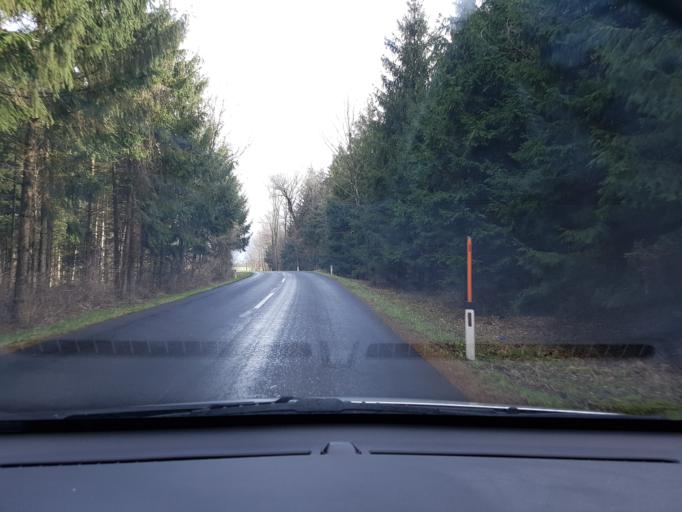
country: AT
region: Upper Austria
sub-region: Politischer Bezirk Linz-Land
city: Sankt Florian
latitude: 48.1703
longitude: 14.3751
